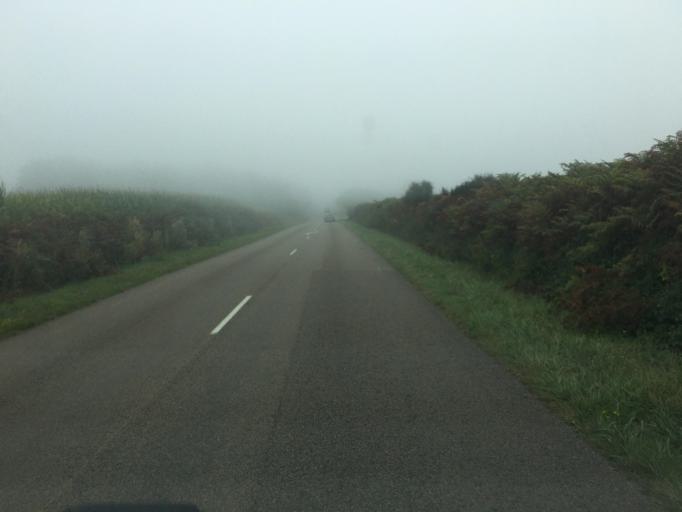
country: FR
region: Brittany
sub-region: Departement du Finistere
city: Plogoff
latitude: 48.0579
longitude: -4.6667
